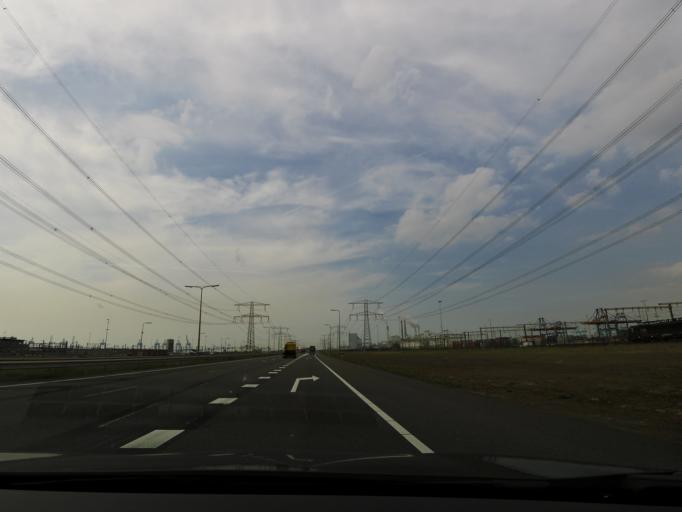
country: NL
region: South Holland
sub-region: Gemeente Rotterdam
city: Hoek van Holland
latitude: 51.9399
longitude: 4.0295
